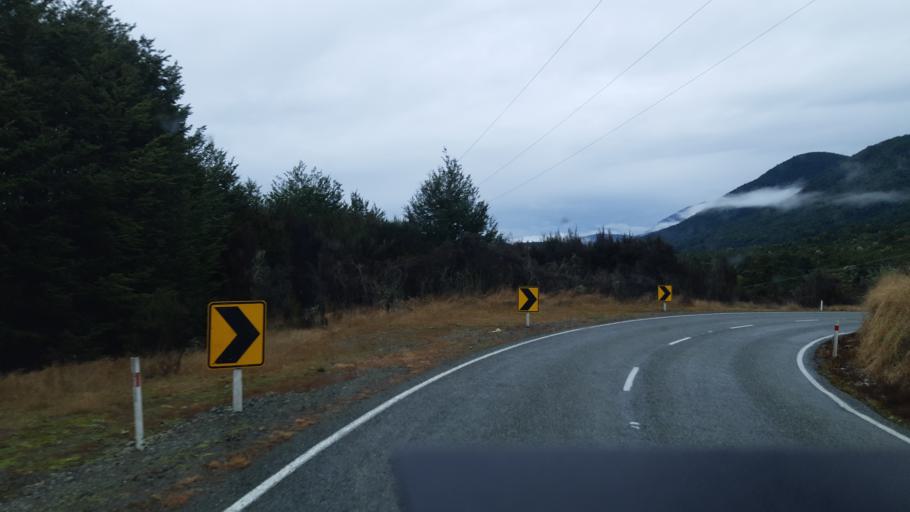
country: NZ
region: Tasman
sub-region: Tasman District
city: Wakefield
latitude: -41.7643
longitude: 172.8930
